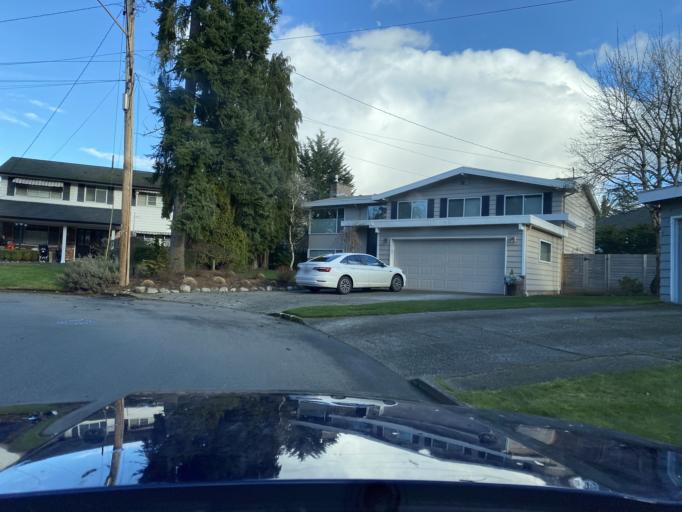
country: US
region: Washington
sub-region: King County
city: Bellevue
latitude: 47.6014
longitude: -122.1930
